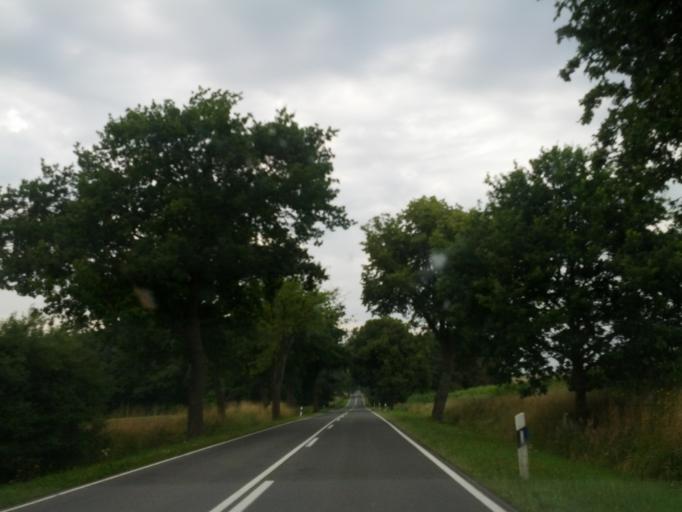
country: DE
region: Mecklenburg-Vorpommern
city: Satow-Oberhagen
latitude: 53.9868
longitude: 11.8542
